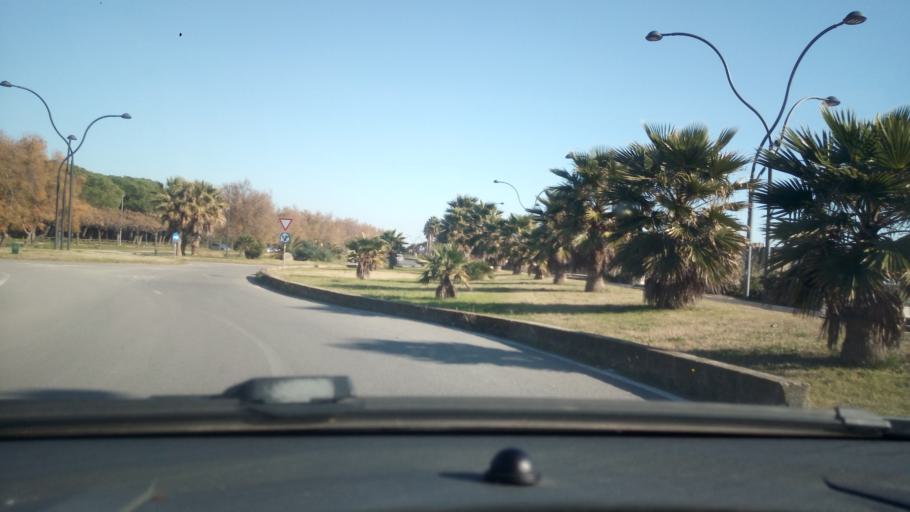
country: IT
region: Calabria
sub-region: Provincia di Catanzaro
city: Barone
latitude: 38.8295
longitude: 16.6396
